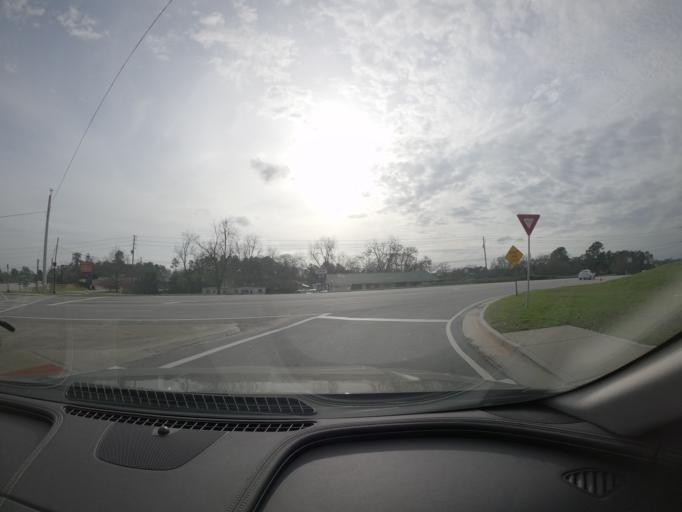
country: US
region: Georgia
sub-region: Columbia County
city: Evans
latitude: 33.4744
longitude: -82.1292
